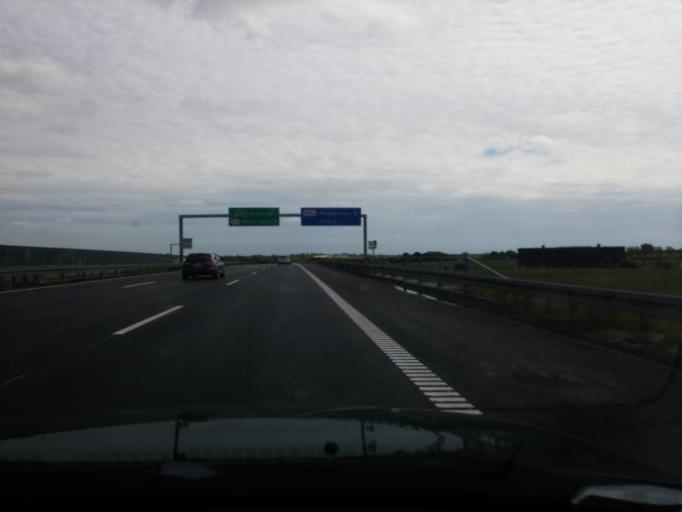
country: DK
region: South Denmark
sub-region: Middelfart Kommune
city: Strib
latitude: 55.5044
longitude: 9.7869
